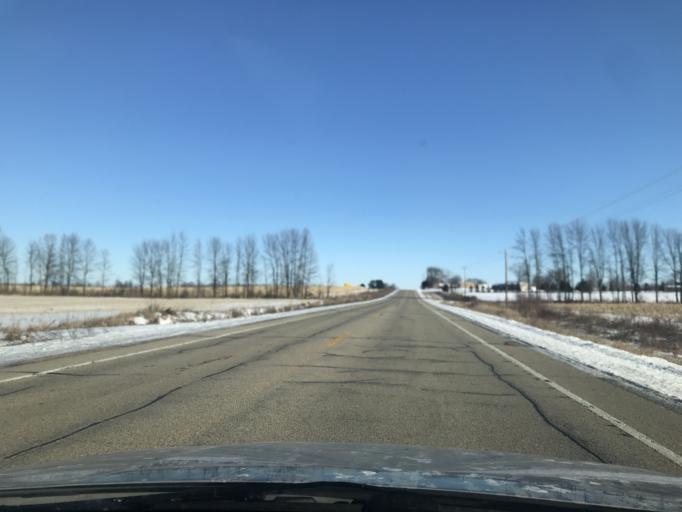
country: US
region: Wisconsin
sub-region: Oconto County
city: Oconto
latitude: 44.8928
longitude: -87.9754
